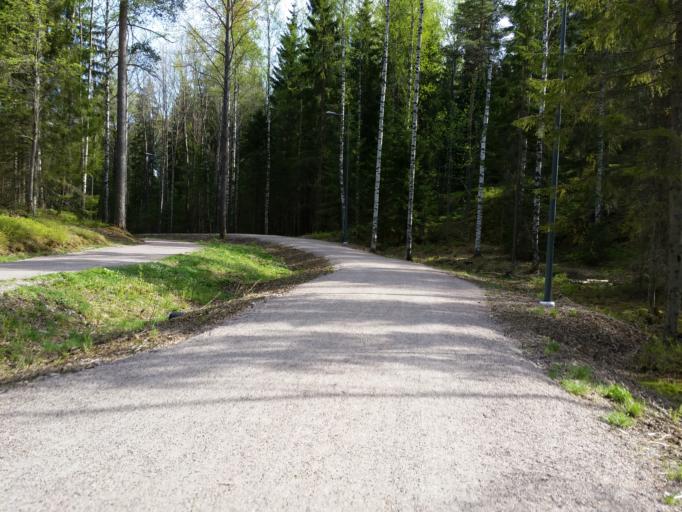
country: FI
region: Uusimaa
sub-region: Helsinki
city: Kauniainen
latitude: 60.1816
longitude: 24.7176
